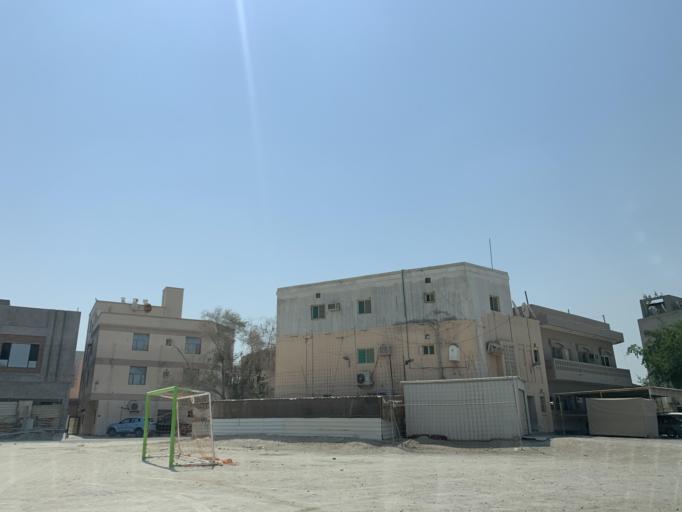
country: BH
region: Manama
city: Jidd Hafs
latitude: 26.2069
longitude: 50.5204
